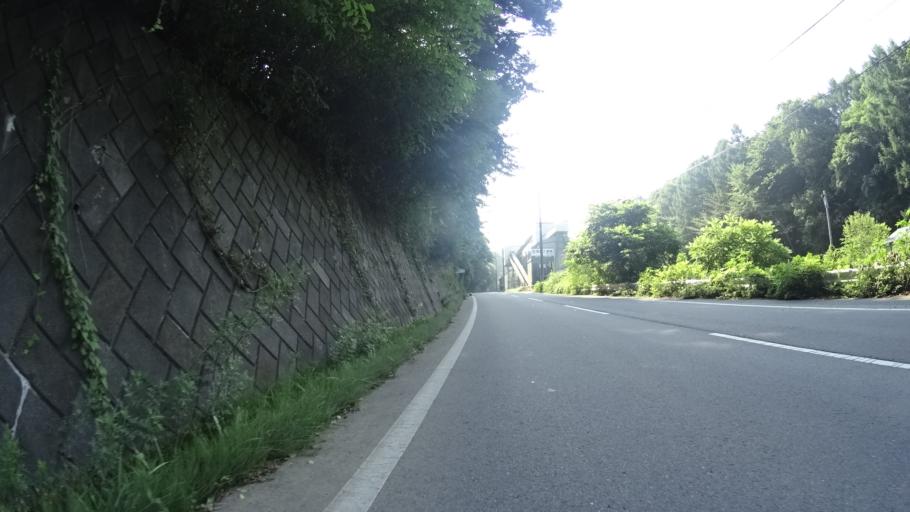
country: JP
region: Nagano
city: Chino
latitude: 35.9744
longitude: 138.1779
